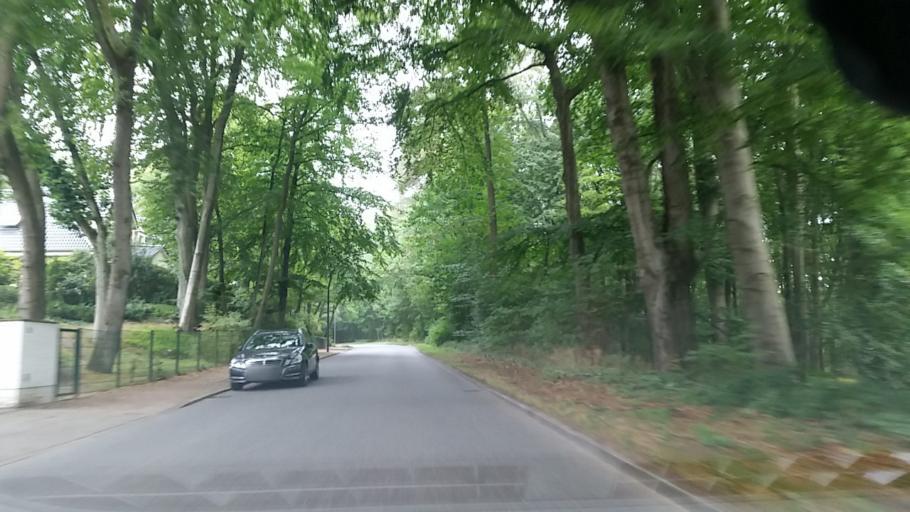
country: DE
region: Schleswig-Holstein
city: Wedel
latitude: 53.5674
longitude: 9.7780
